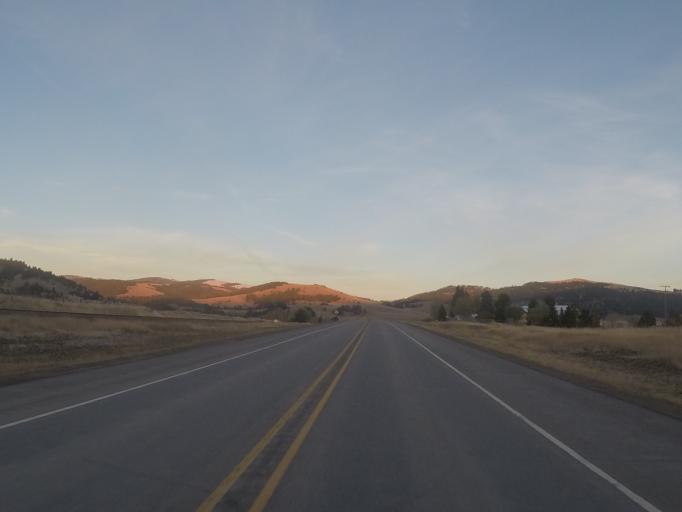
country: US
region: Montana
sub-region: Lewis and Clark County
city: Helena West Side
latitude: 46.5567
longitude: -112.4064
